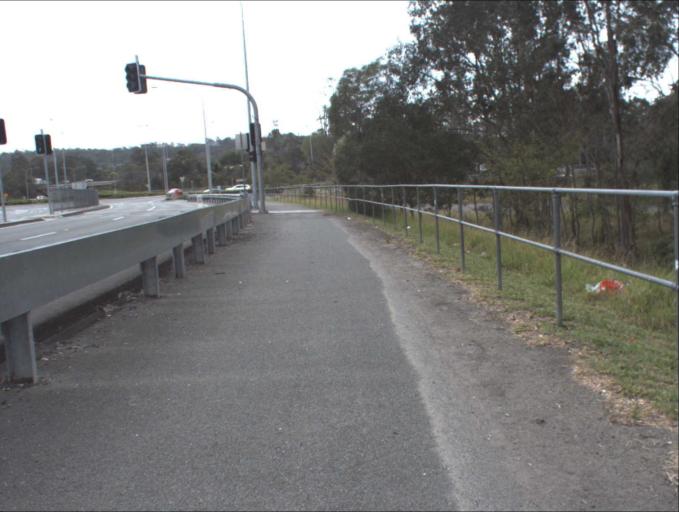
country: AU
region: Queensland
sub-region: Logan
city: Slacks Creek
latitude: -27.6401
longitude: 153.1365
